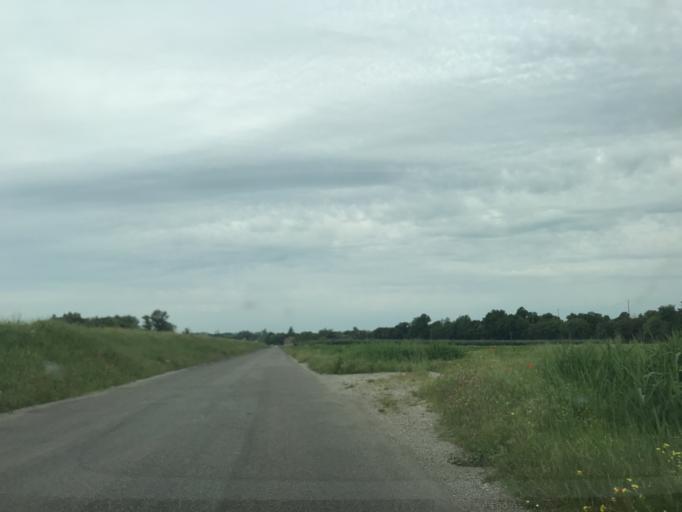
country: FR
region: Provence-Alpes-Cote d'Azur
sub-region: Departement des Alpes-de-Haute-Provence
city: Volx
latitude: 43.8438
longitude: 5.8322
